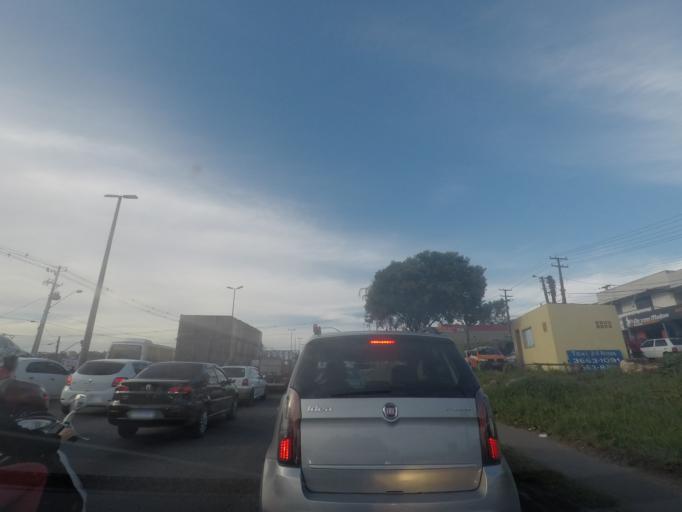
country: BR
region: Parana
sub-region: Pinhais
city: Pinhais
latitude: -25.3741
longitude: -49.1931
